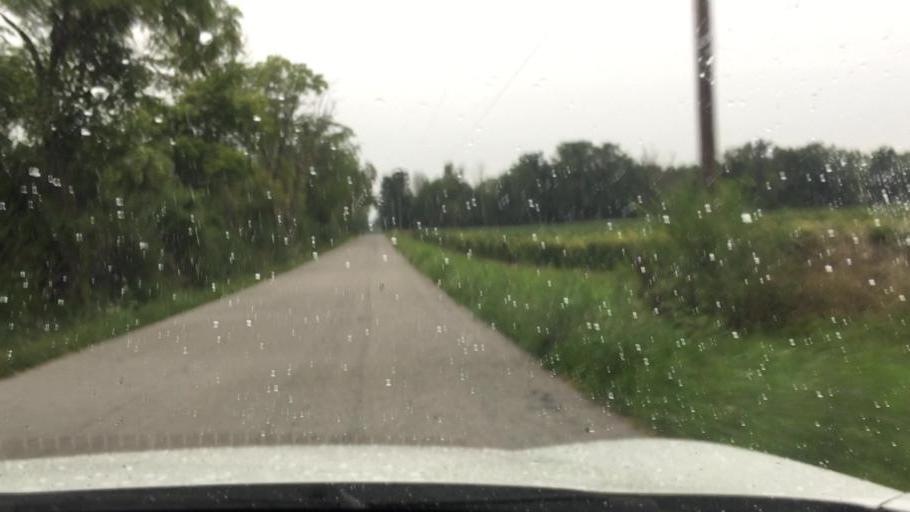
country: US
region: Ohio
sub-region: Champaign County
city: Mechanicsburg
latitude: 40.0146
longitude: -83.6425
